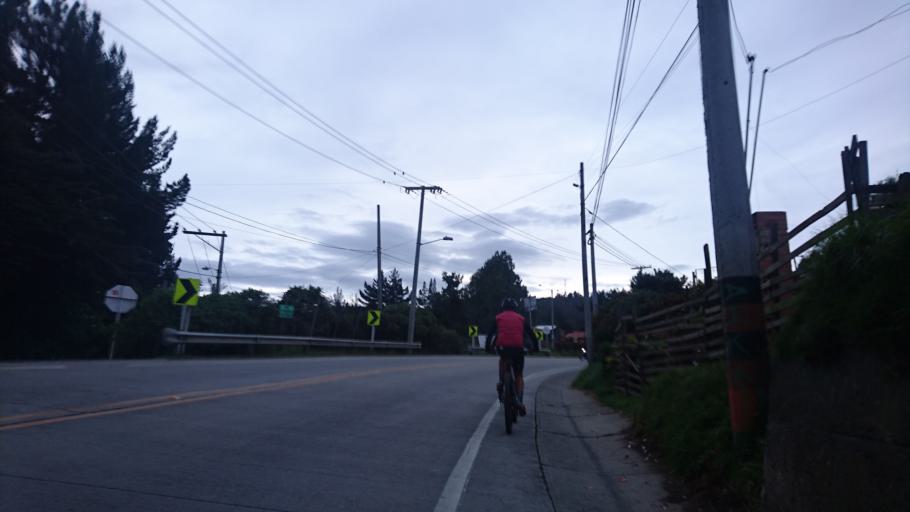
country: CO
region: Bogota D.C.
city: Barrio San Luis
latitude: 4.6725
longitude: -74.0173
